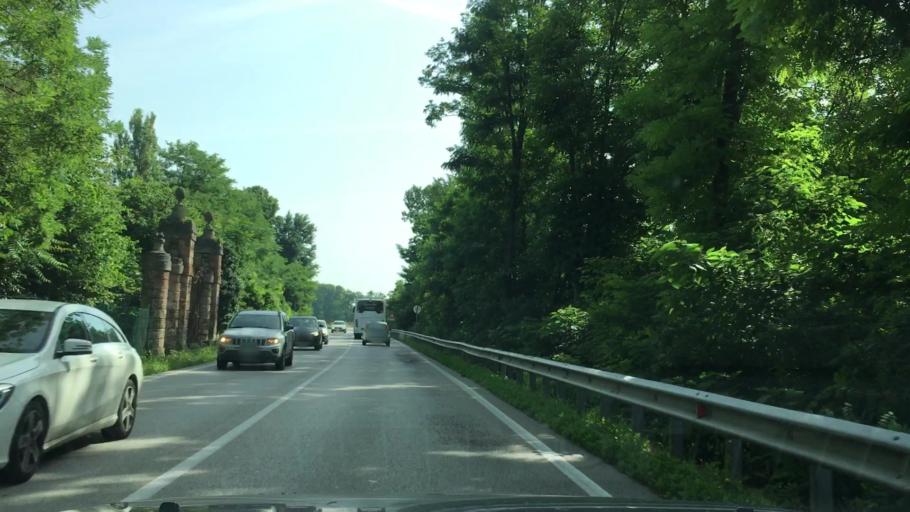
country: IT
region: Emilia-Romagna
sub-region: Provincia di Bologna
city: Progresso
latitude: 44.5493
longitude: 11.3833
